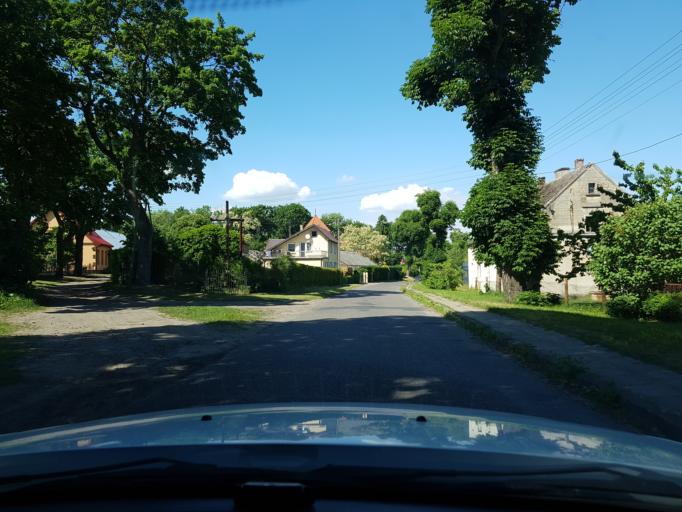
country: PL
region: West Pomeranian Voivodeship
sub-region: Powiat gryfinski
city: Gryfino
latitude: 53.1740
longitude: 14.5417
